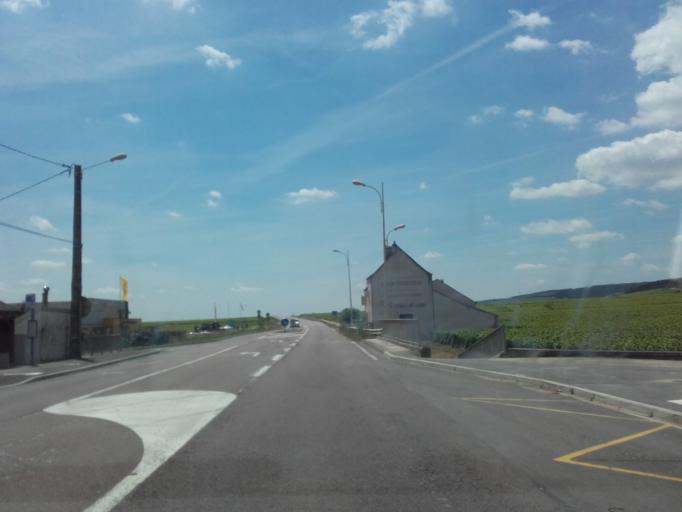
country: FR
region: Bourgogne
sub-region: Departement de la Cote-d'Or
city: Gevrey-Chambertin
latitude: 47.1936
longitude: 4.9688
